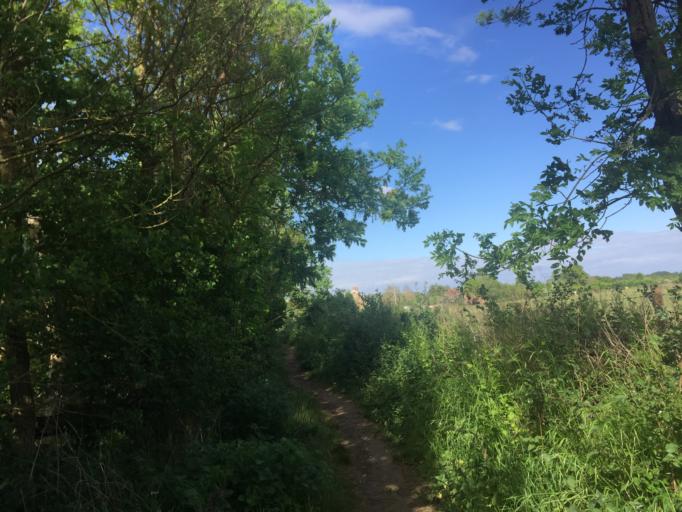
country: GB
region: England
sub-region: Royal Borough of Windsor and Maidenhead
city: Bray
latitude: 51.5074
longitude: -0.6674
